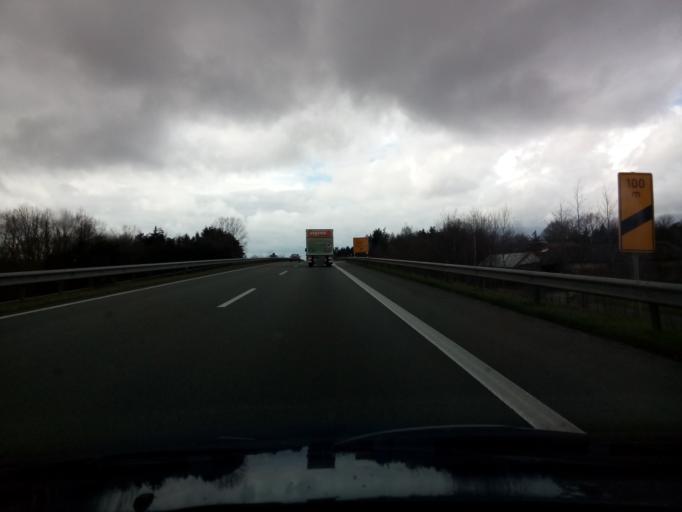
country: DE
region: Lower Saxony
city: Twist
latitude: 52.7225
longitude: 7.1035
